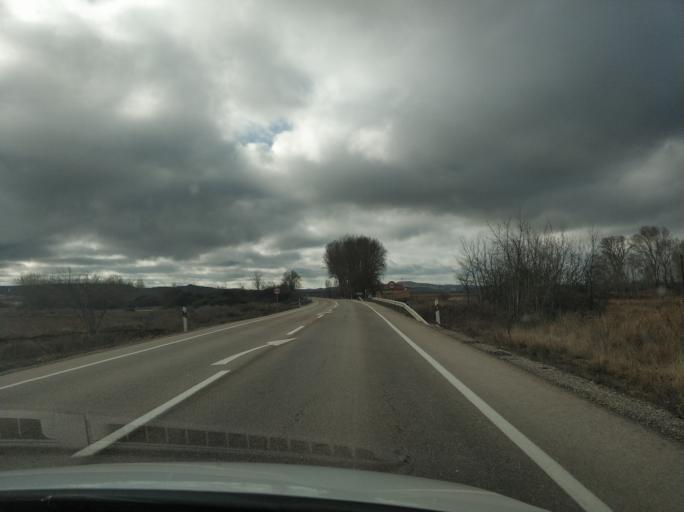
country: ES
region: Castille and Leon
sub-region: Provincia de Soria
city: San Esteban de Gormaz
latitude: 41.5700
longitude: -3.2175
